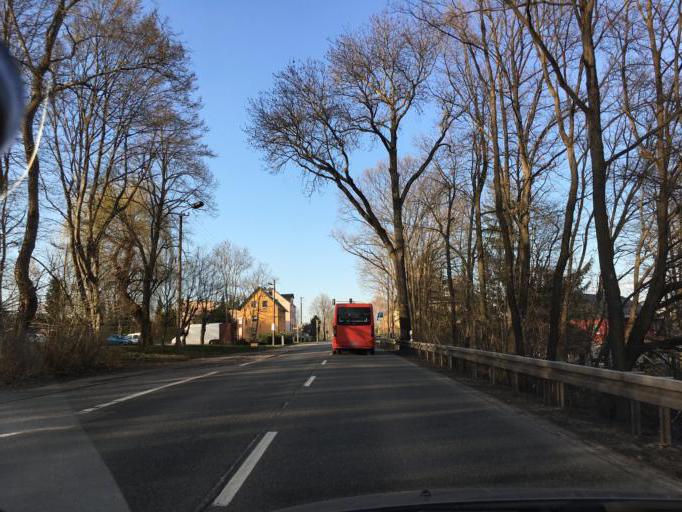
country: DE
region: Saxony
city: Limbach-Oberfrohna
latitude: 50.8659
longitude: 12.7728
